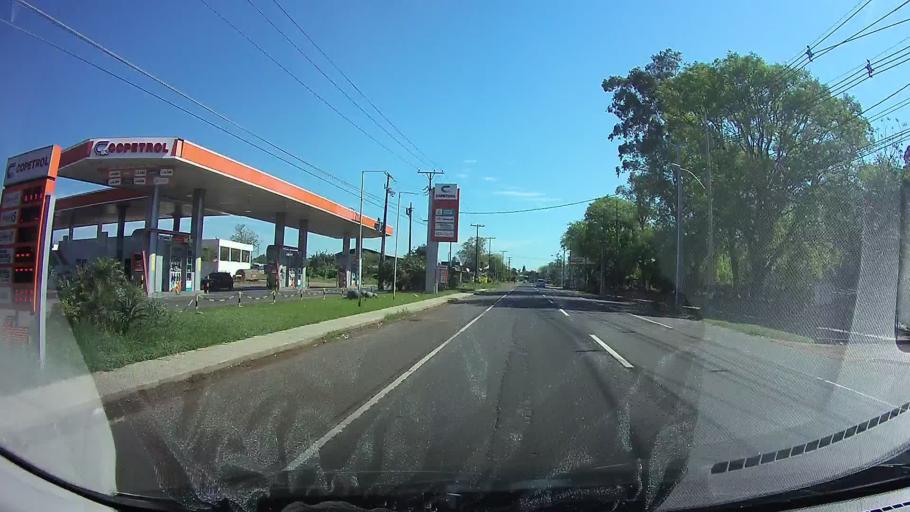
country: PY
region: Central
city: Ypacarai
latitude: -25.3943
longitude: -57.2787
